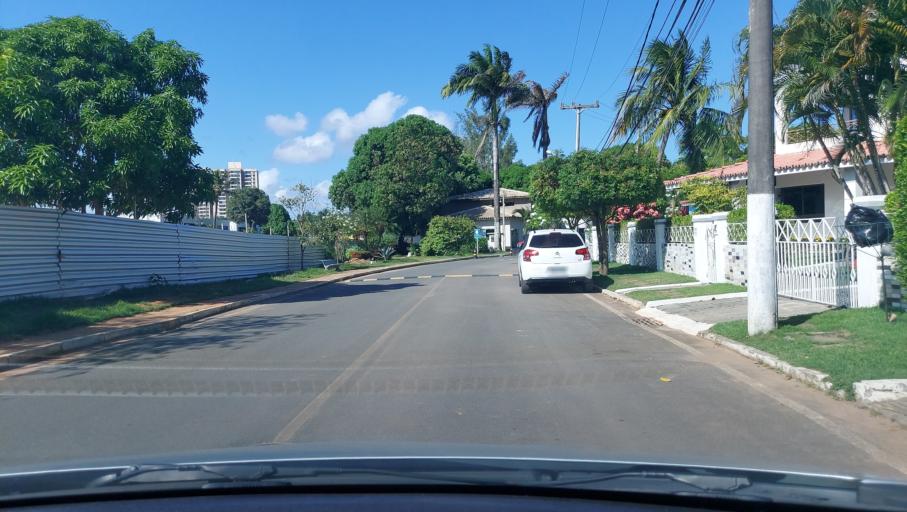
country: BR
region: Bahia
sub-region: Lauro De Freitas
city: Lauro de Freitas
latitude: -12.9431
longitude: -38.3843
